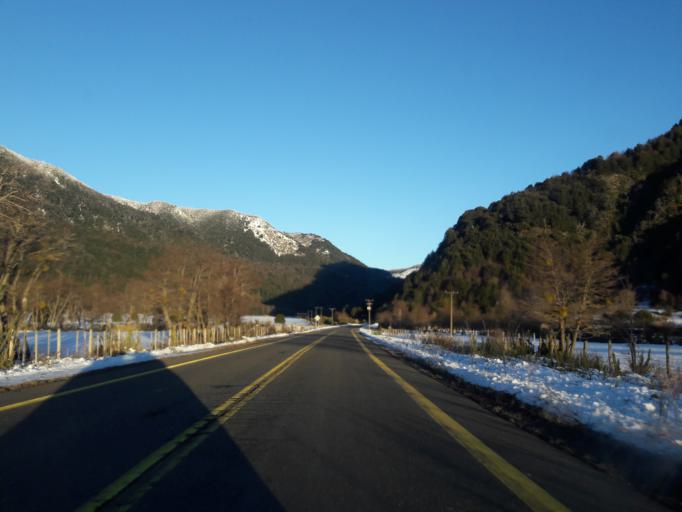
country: CL
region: Araucania
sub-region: Provincia de Cautin
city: Vilcun
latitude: -38.4847
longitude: -71.5313
